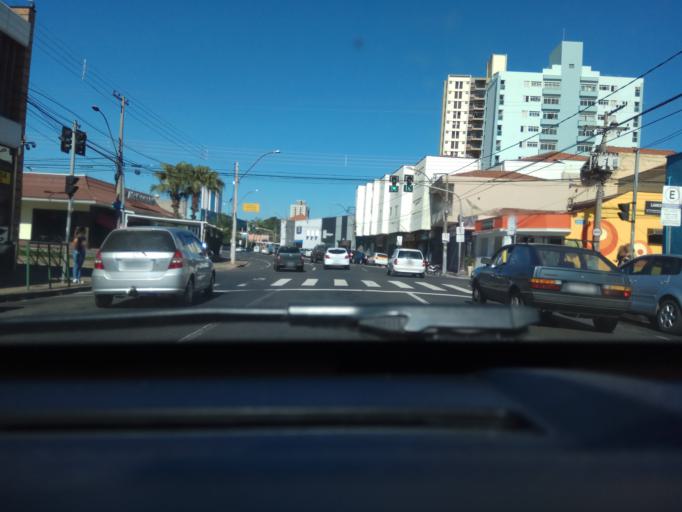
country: BR
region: Sao Paulo
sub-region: Piracicaba
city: Piracicaba
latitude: -22.7297
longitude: -47.6481
